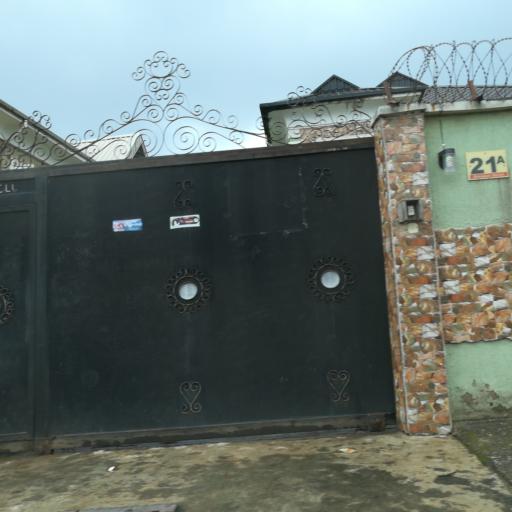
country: NG
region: Lagos
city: Agege
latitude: 6.5990
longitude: 3.2973
